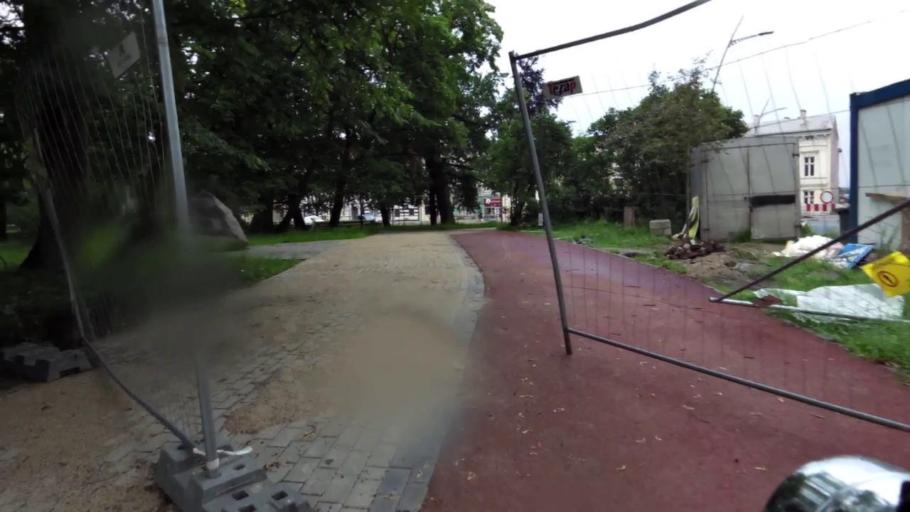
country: PL
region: West Pomeranian Voivodeship
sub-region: Koszalin
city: Koszalin
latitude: 54.1898
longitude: 16.1943
